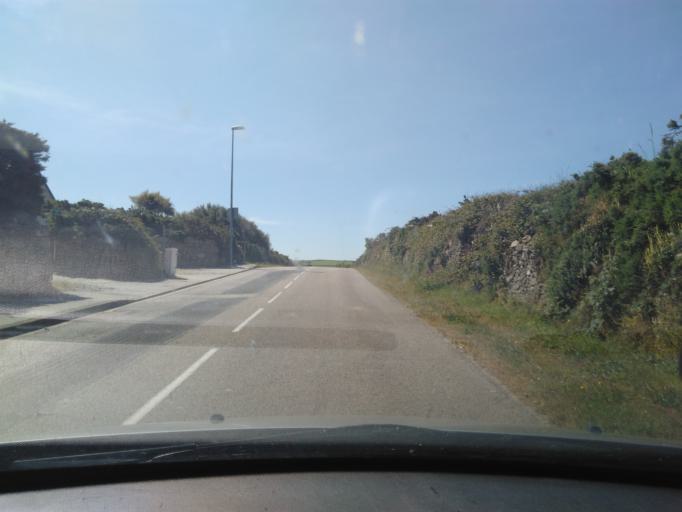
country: FR
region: Lower Normandy
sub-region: Departement de la Manche
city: Beaumont-Hague
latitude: 49.7079
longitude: -1.9319
